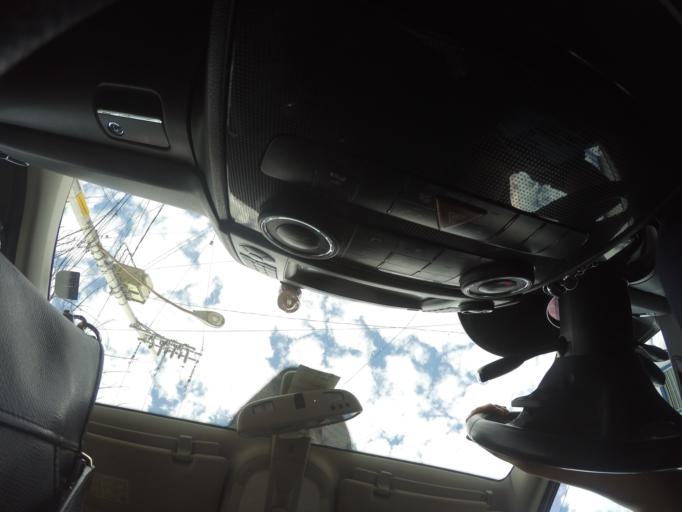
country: MX
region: Guanajuato
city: Leon
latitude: 21.1161
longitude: -101.6500
